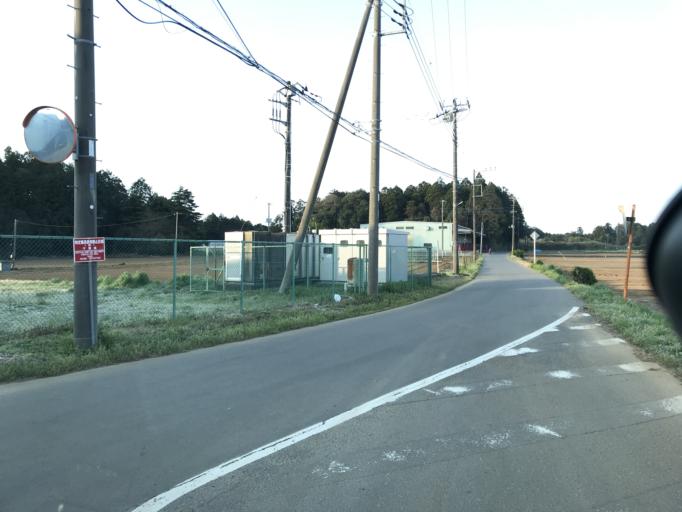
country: JP
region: Chiba
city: Omigawa
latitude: 35.7936
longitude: 140.5486
